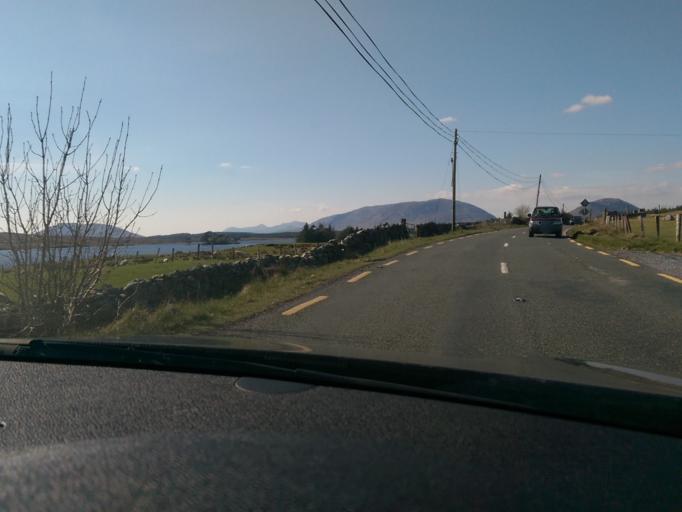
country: IE
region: Connaught
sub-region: County Galway
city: Oughterard
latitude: 53.4371
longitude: -9.4428
